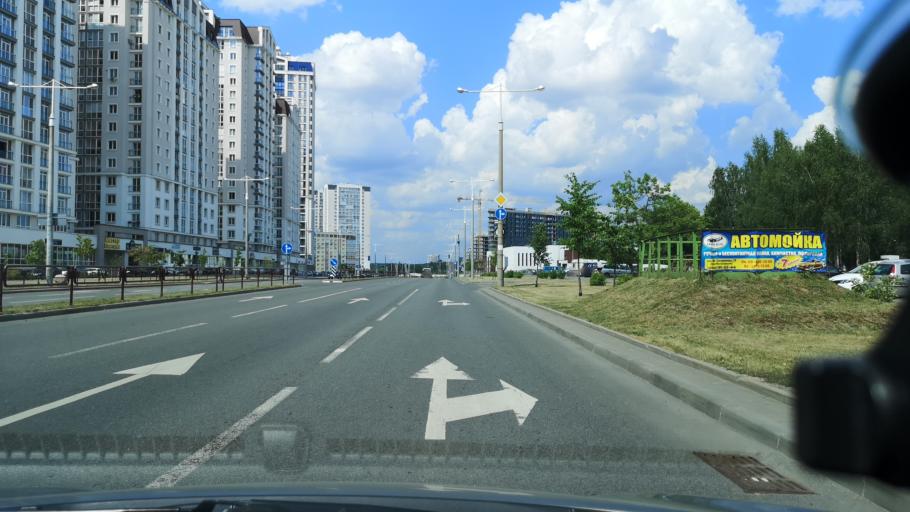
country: BY
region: Minsk
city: Borovlyany
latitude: 53.9287
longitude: 27.6556
